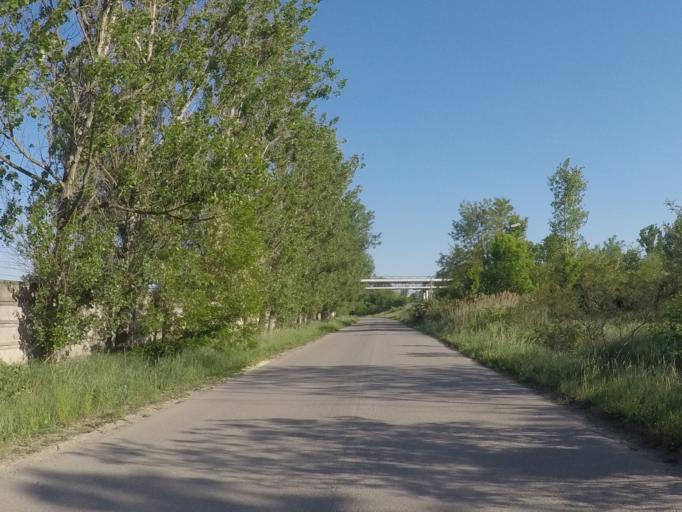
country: HU
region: Borsod-Abauj-Zemplen
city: Mucsony
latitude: 48.2364
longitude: 20.6793
